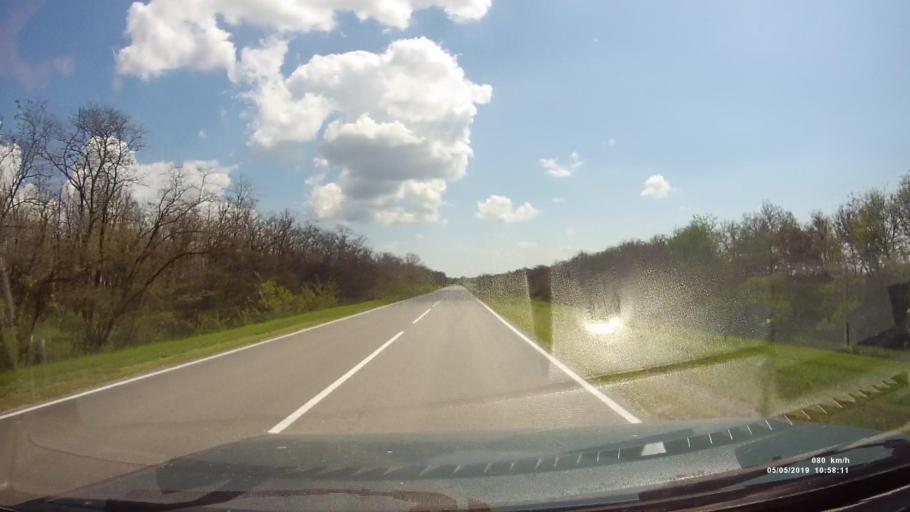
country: RU
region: Rostov
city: Ust'-Donetskiy
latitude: 47.6703
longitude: 40.8486
